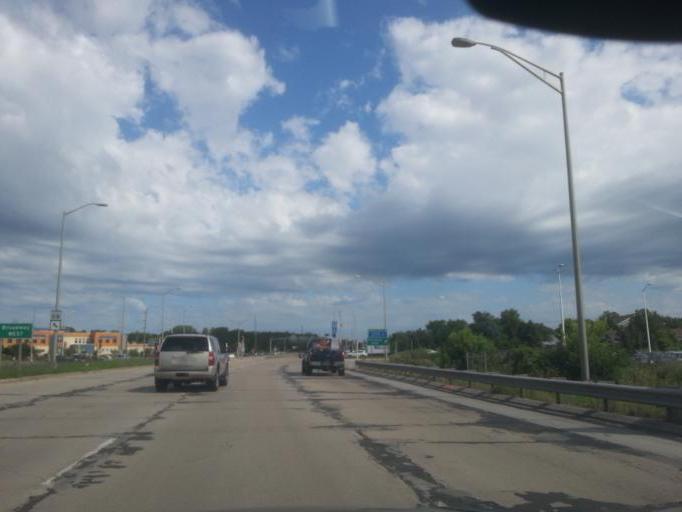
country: US
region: Wisconsin
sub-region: Dane County
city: Monona
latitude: 43.0468
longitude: -89.3074
